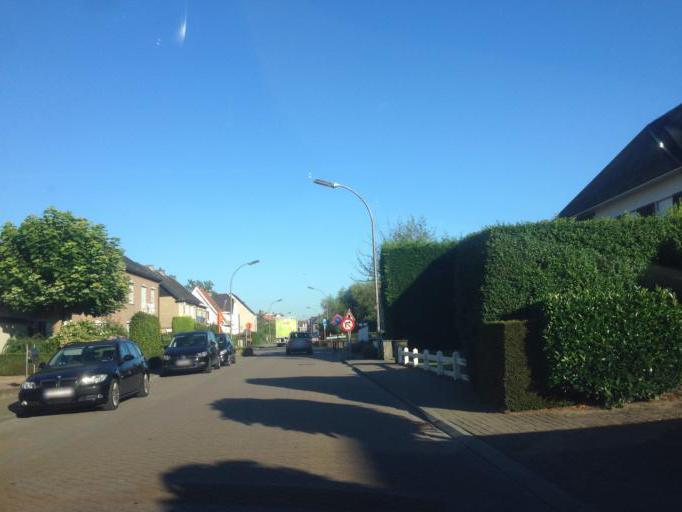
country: BE
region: Flanders
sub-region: Provincie Antwerpen
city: Geel
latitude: 51.1654
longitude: 4.9936
